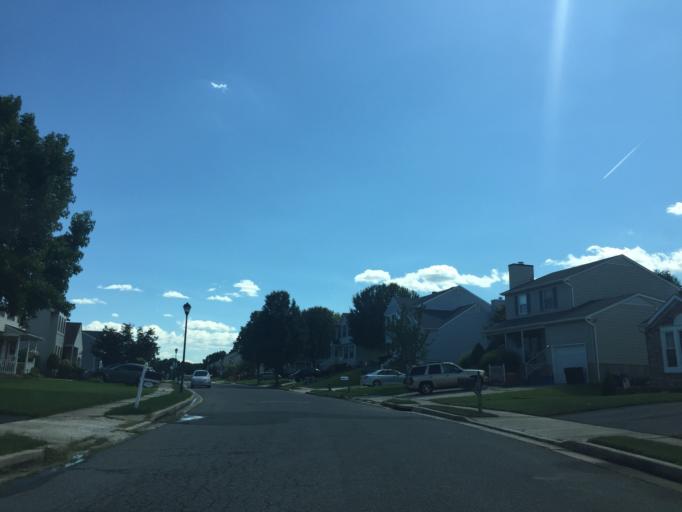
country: US
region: Maryland
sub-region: Baltimore County
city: Perry Hall
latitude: 39.4062
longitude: -76.4672
